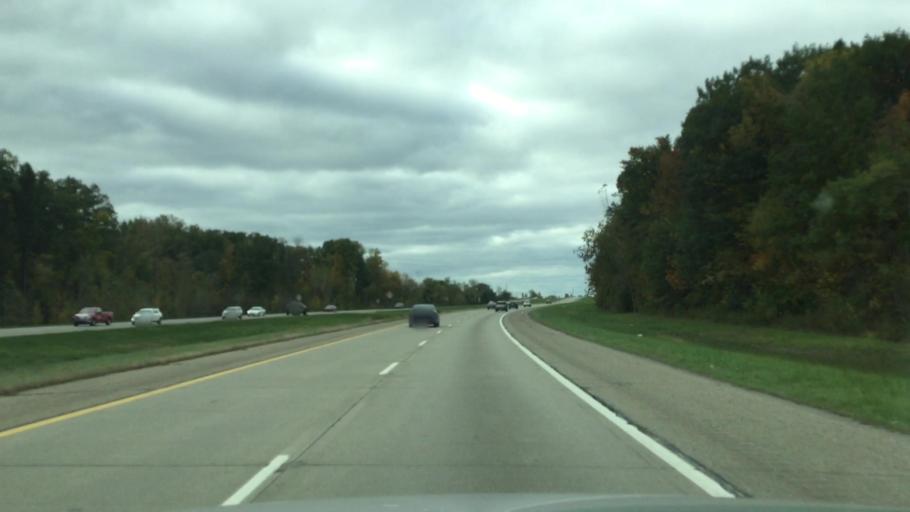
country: US
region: Michigan
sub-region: Macomb County
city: Romeo
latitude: 42.7947
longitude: -83.0015
